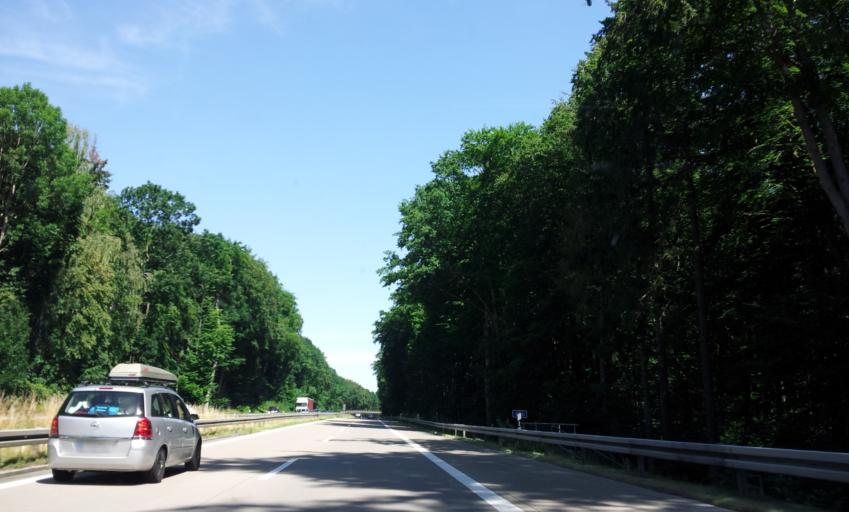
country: DE
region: Brandenburg
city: Gramzow
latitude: 53.1469
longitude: 13.8982
